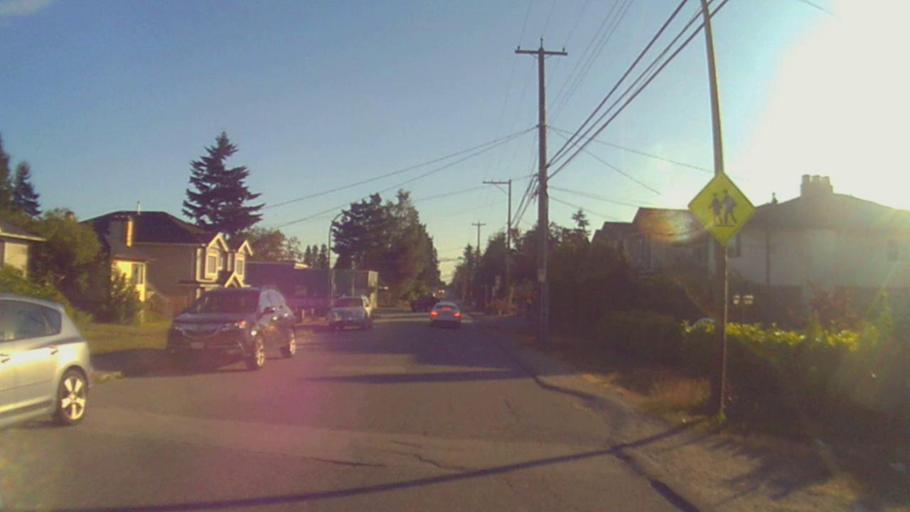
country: CA
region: British Columbia
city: New Westminster
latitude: 49.2242
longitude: -122.9227
